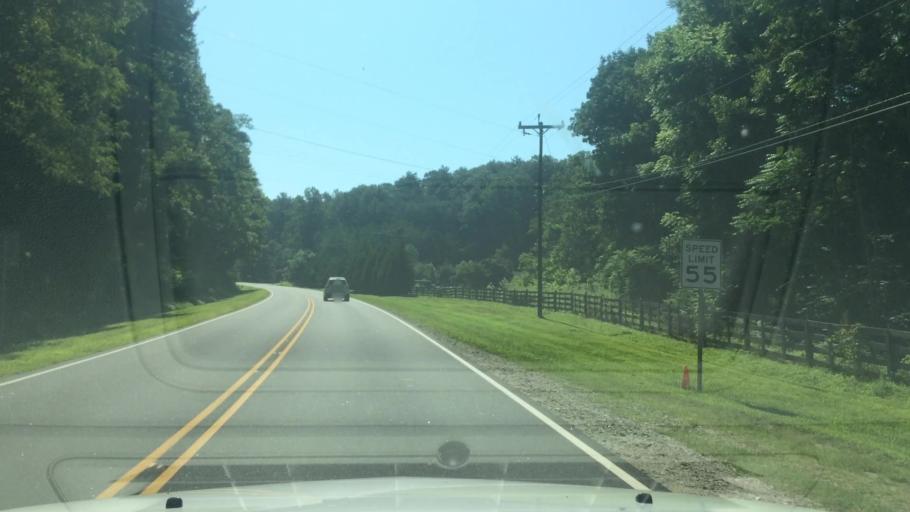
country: US
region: North Carolina
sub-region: Caldwell County
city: Lenoir
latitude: 35.9146
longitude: -81.4809
